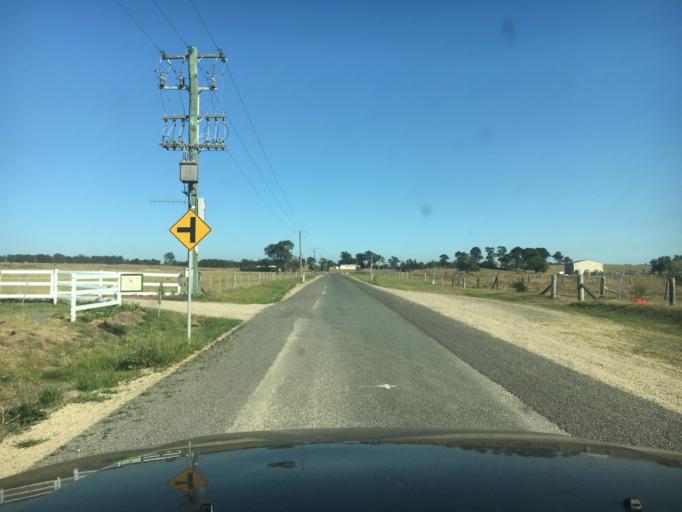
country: AU
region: New South Wales
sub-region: Cessnock
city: Branxton
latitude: -32.5583
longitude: 151.2869
